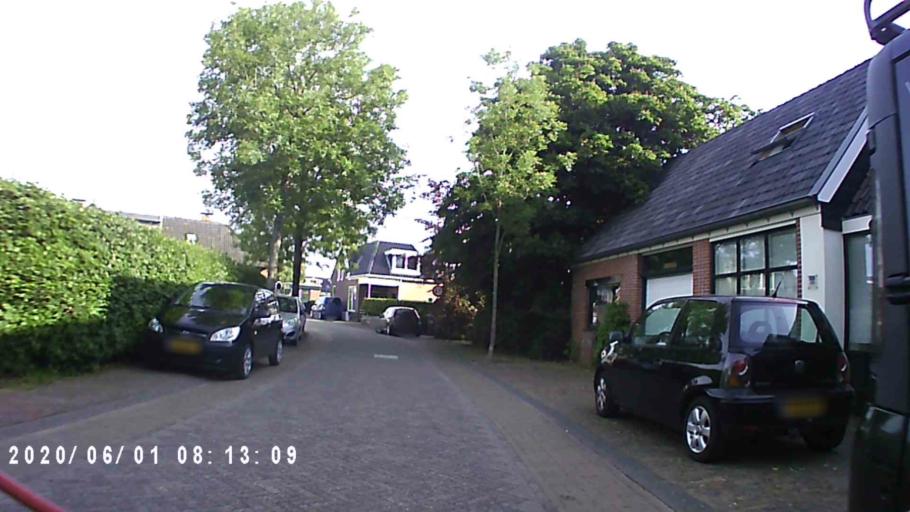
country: NL
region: Friesland
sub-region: Gemeente Ferwerderadiel
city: Burdaard
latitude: 53.2945
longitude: 5.8801
